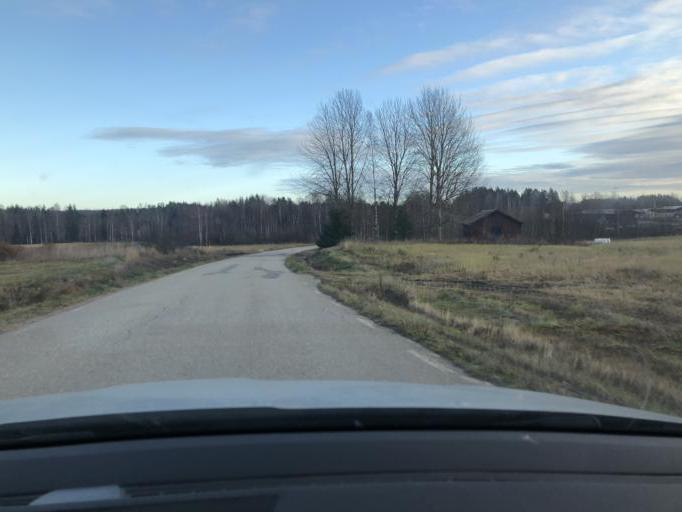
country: SE
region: Gaevleborg
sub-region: Hudiksvalls Kommun
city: Sorforsa
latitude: 61.7124
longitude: 16.9420
